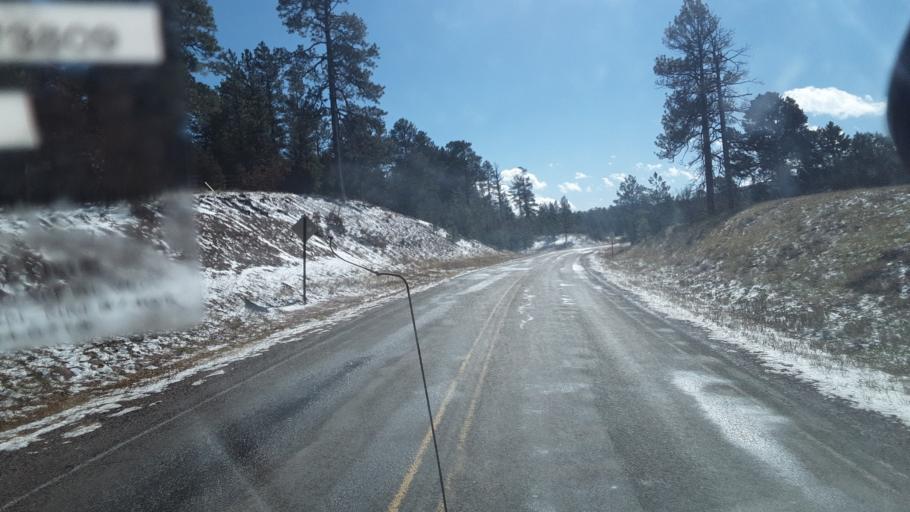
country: US
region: New Mexico
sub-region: Rio Arriba County
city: Santa Teresa
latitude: 36.2093
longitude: -106.7758
